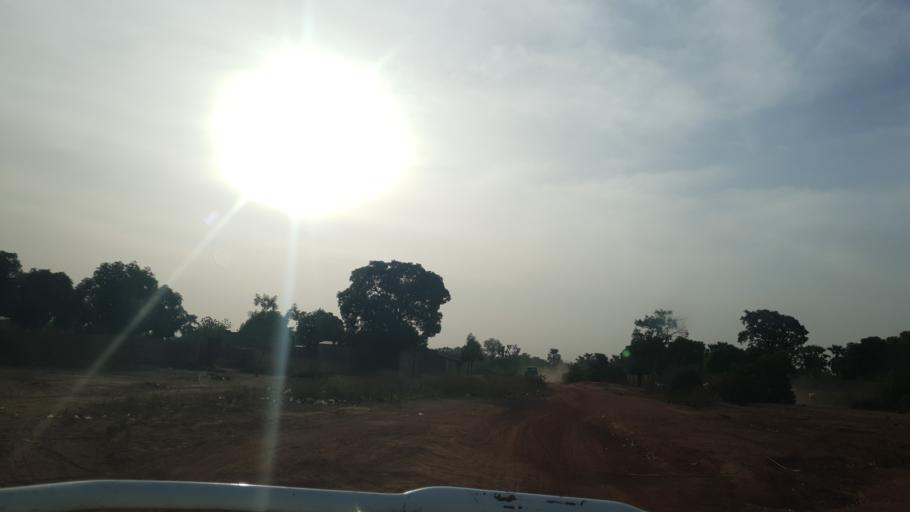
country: ML
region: Segou
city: Baroueli
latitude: 12.7726
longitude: -6.9355
